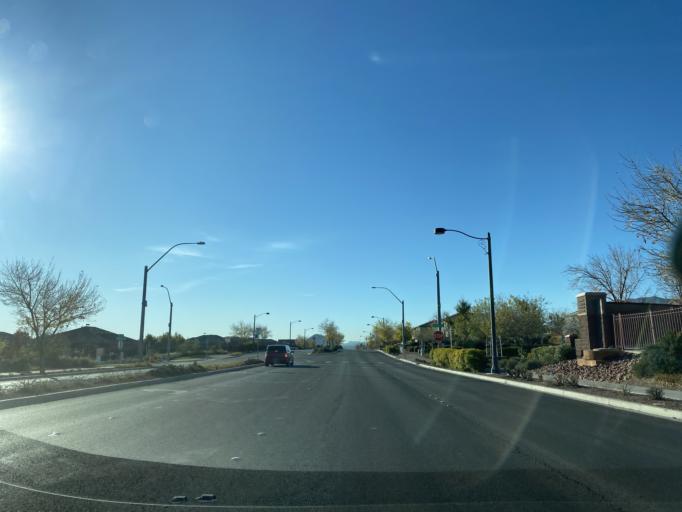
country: US
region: Nevada
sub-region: Clark County
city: Summerlin South
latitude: 36.2927
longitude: -115.3196
